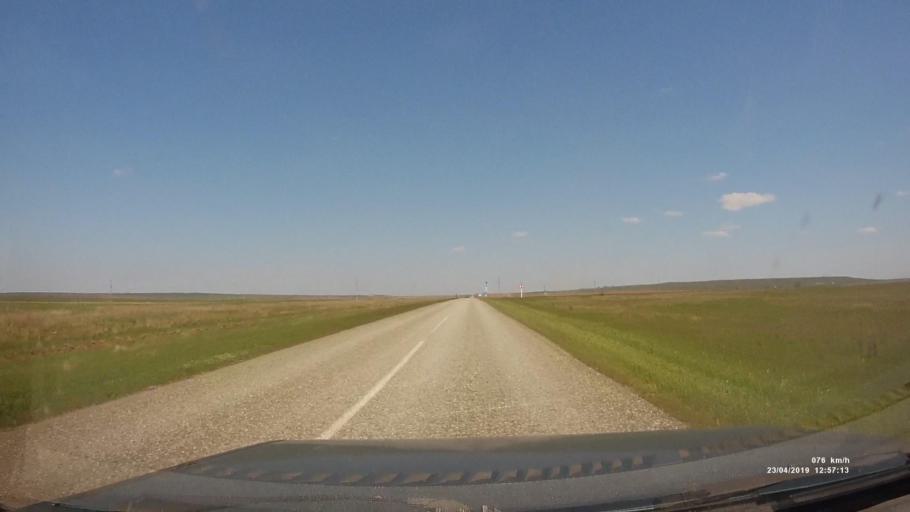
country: RU
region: Kalmykiya
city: Yashalta
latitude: 46.6018
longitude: 42.5792
